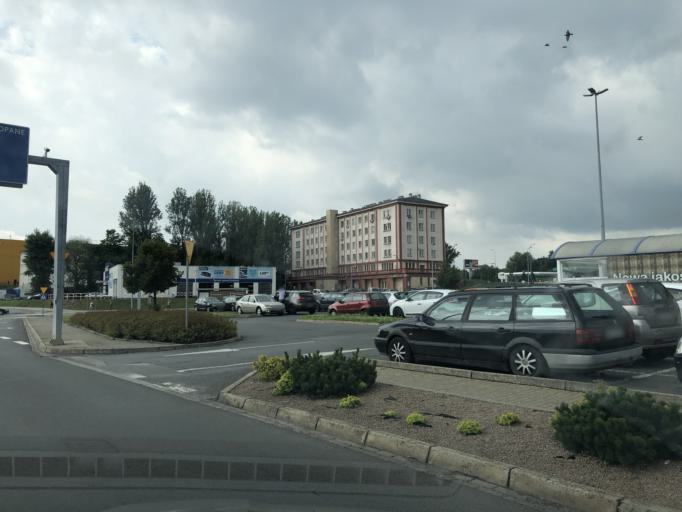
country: PL
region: Lesser Poland Voivodeship
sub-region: Krakow
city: Krakow
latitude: 50.0140
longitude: 19.9304
